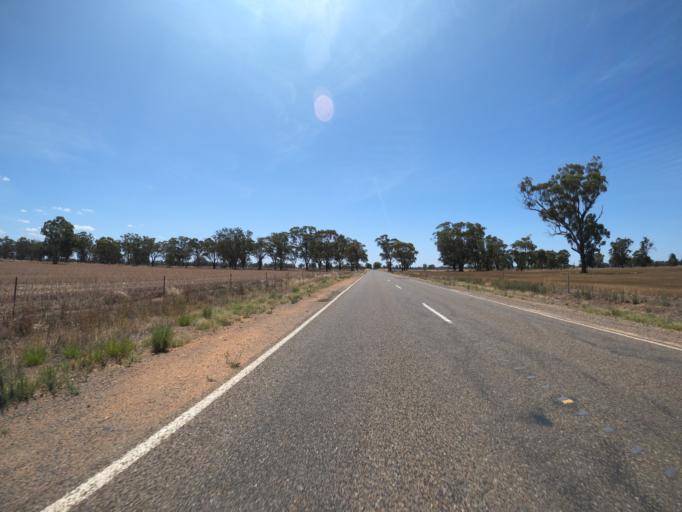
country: AU
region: Victoria
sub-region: Moira
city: Yarrawonga
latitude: -36.1806
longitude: 145.9672
